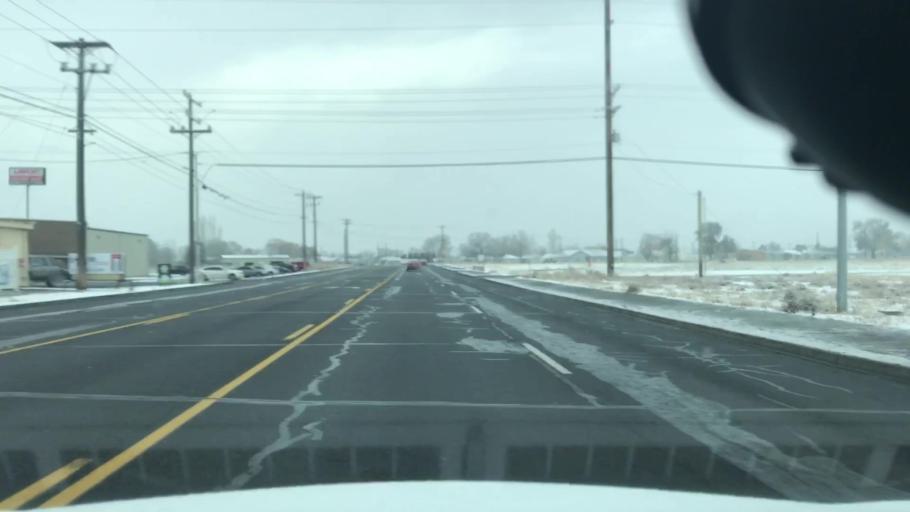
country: US
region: Washington
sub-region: Grant County
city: Moses Lake North
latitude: 47.1807
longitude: -119.3227
